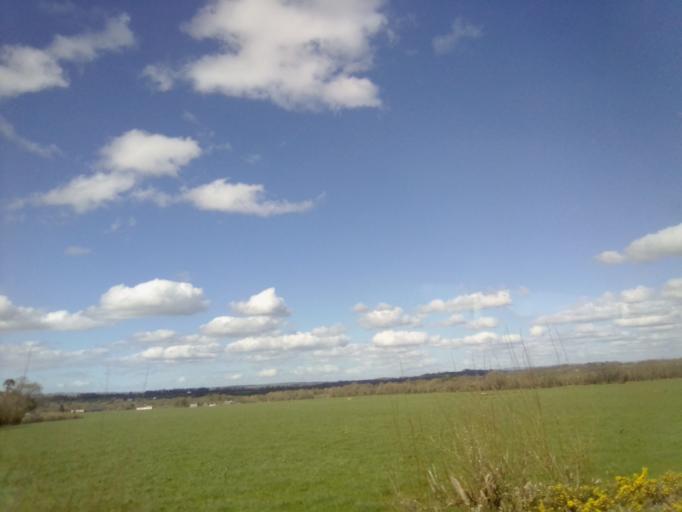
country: IE
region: Munster
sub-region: County Cork
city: Kanturk
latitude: 52.1293
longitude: -8.8383
